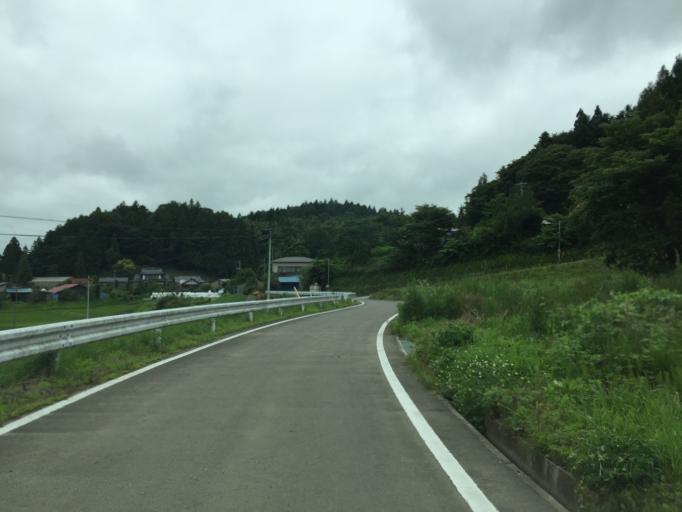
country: JP
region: Fukushima
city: Ishikawa
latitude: 37.2050
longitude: 140.6020
